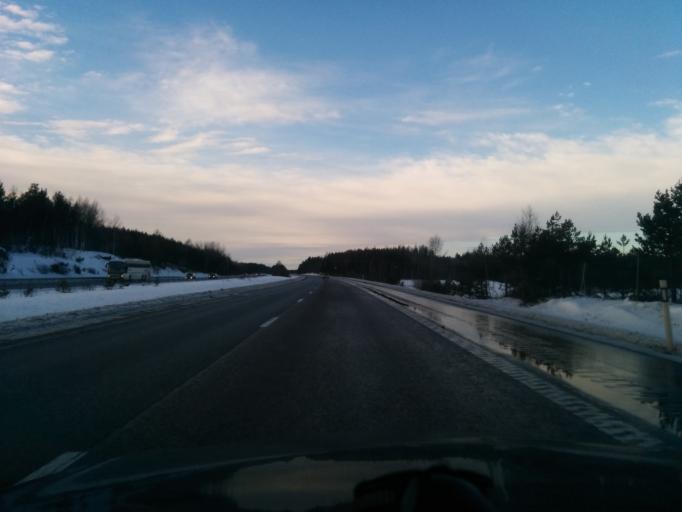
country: SE
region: Uppsala
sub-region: Habo Kommun
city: Balsta
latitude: 59.6054
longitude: 17.4309
